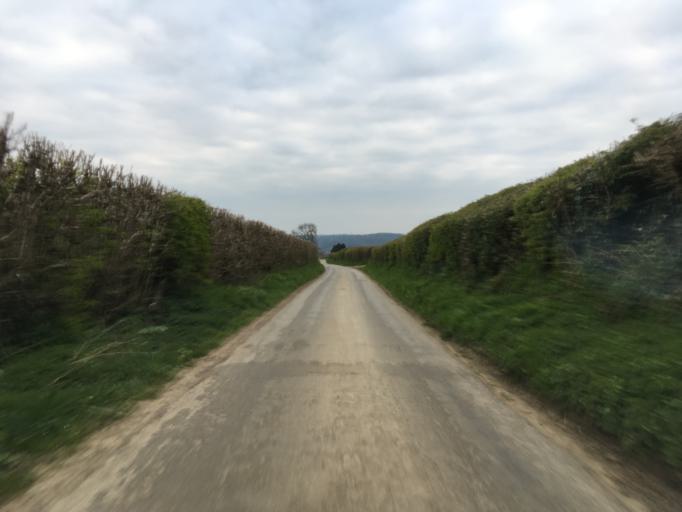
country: GB
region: England
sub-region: South Gloucestershire
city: Horton
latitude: 51.5916
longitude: -2.3403
